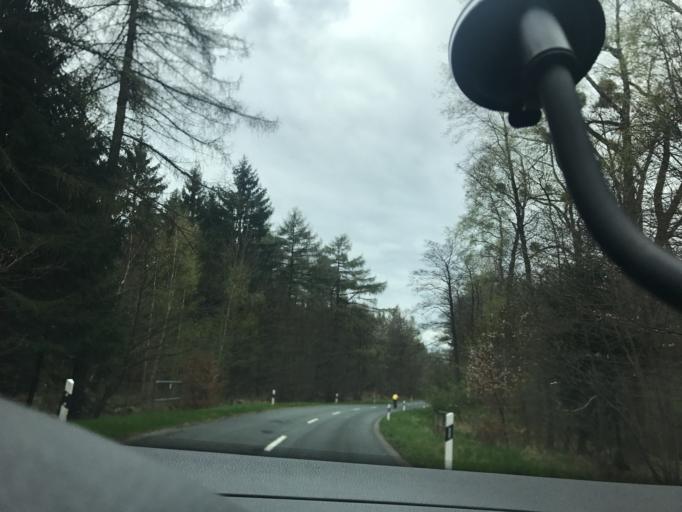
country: DE
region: Lower Saxony
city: Rabke
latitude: 52.1652
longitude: 10.8787
